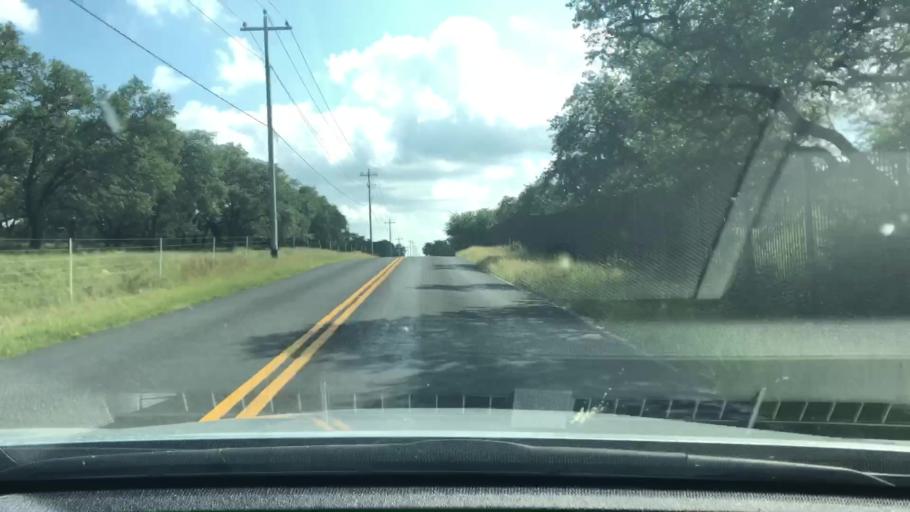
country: US
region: Texas
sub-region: Bexar County
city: Fair Oaks Ranch
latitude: 29.7807
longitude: -98.6266
